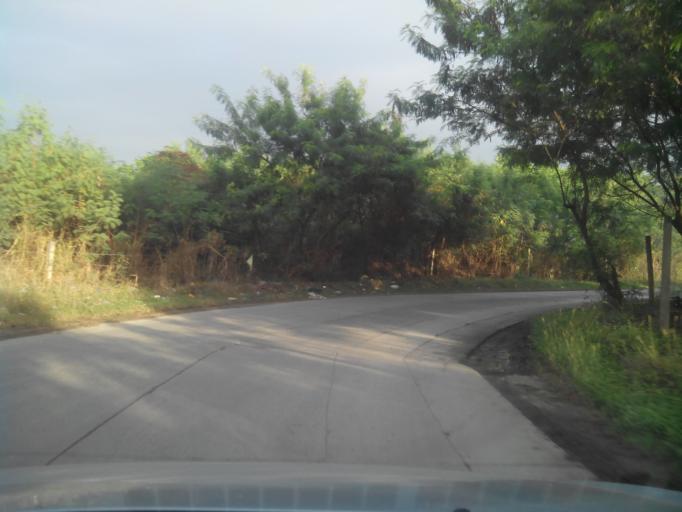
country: PH
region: Calabarzon
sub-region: Province of Rizal
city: Taytay
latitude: 14.5562
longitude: 121.1222
